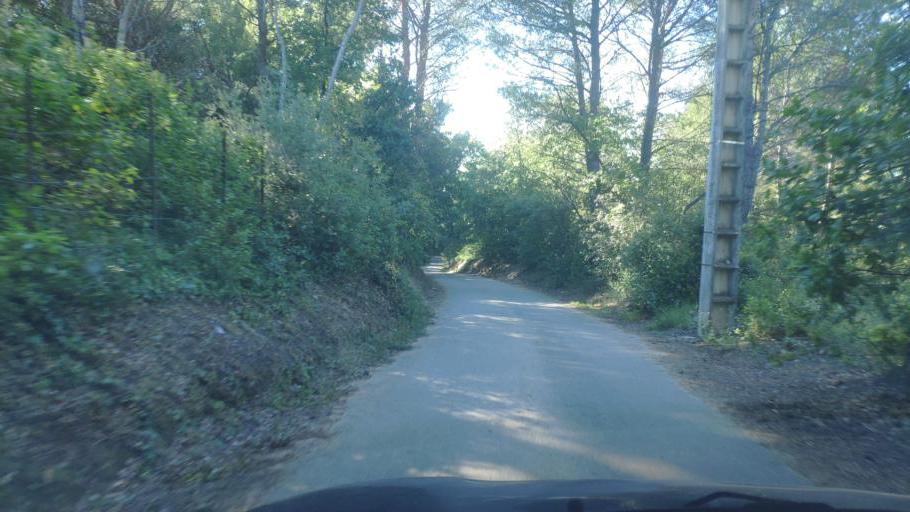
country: FR
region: Provence-Alpes-Cote d'Azur
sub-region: Departement du Vaucluse
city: Aubignan
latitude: 44.0836
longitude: 5.0424
